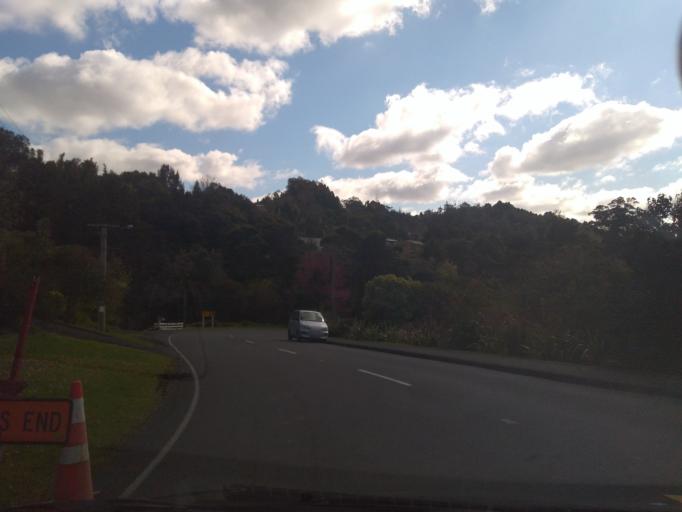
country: NZ
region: Northland
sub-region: Whangarei
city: Whangarei
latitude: -35.7025
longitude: 174.3292
